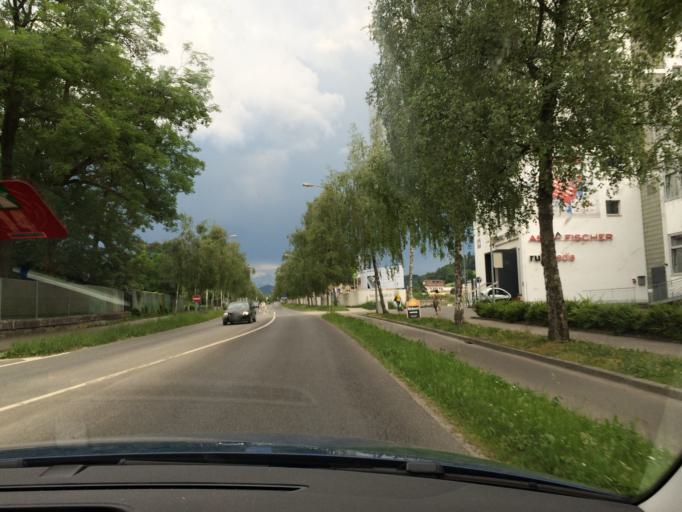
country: CH
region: Bern
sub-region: Bern-Mittelland District
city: Kehrsatz
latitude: 46.9266
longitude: 7.4553
